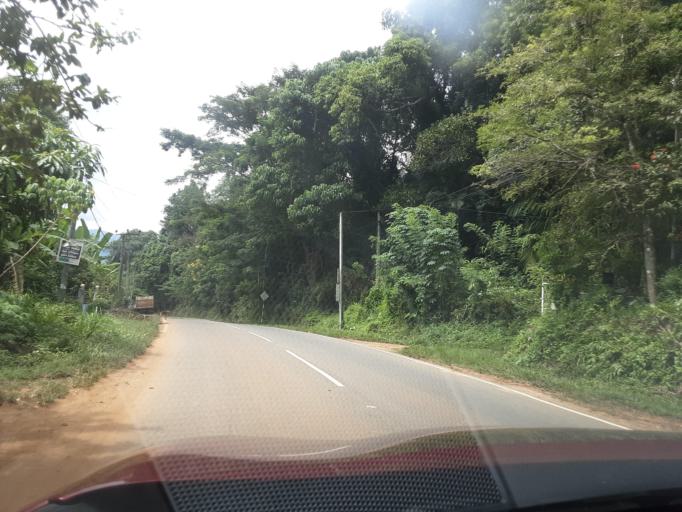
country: LK
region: Uva
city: Monaragala
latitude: 6.8960
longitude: 81.2461
